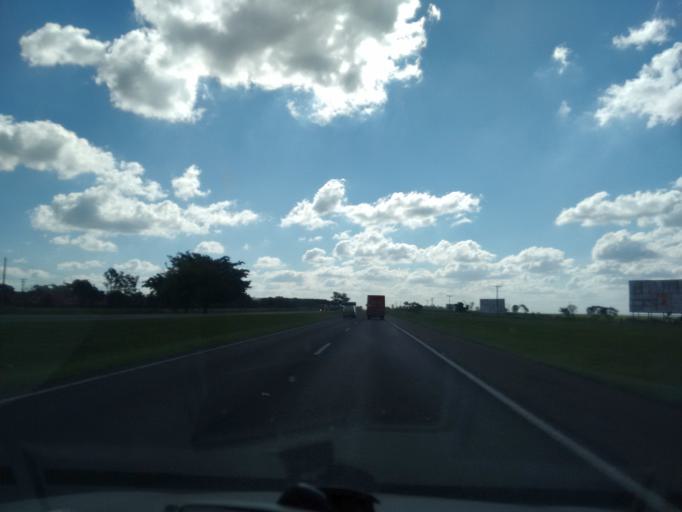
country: BR
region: Sao Paulo
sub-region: Ibate
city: Ibate
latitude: -21.9332
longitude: -48.0168
